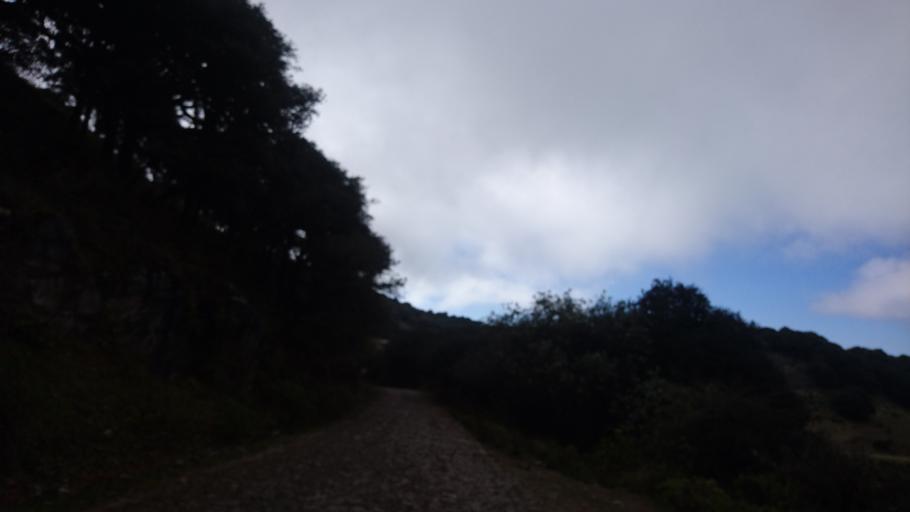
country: MX
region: San Luis Potosi
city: Zaragoza
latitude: 22.0691
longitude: -100.6400
